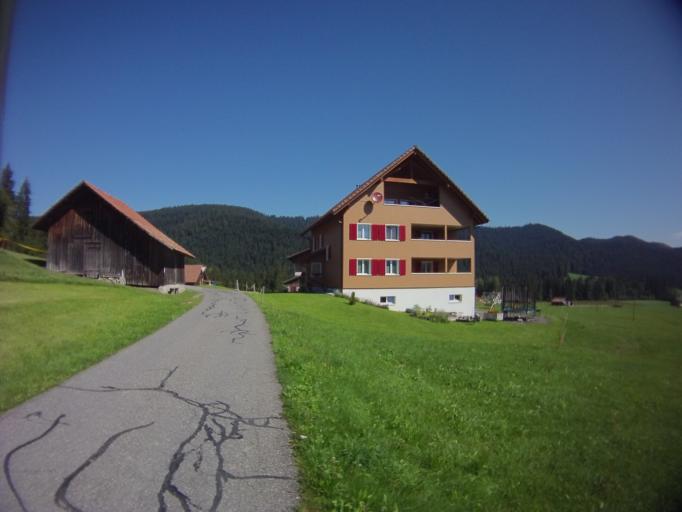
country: CH
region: Schwyz
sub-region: Bezirk Schwyz
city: Rothenthurm
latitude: 47.1436
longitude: 8.6832
